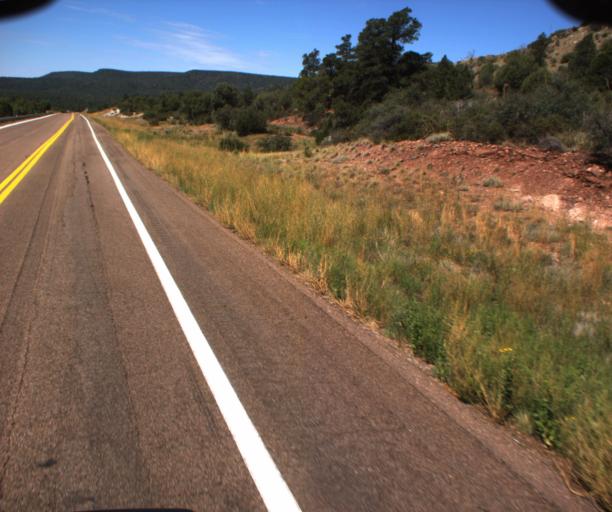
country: US
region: Arizona
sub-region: Navajo County
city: Cibecue
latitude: 33.8724
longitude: -110.4007
